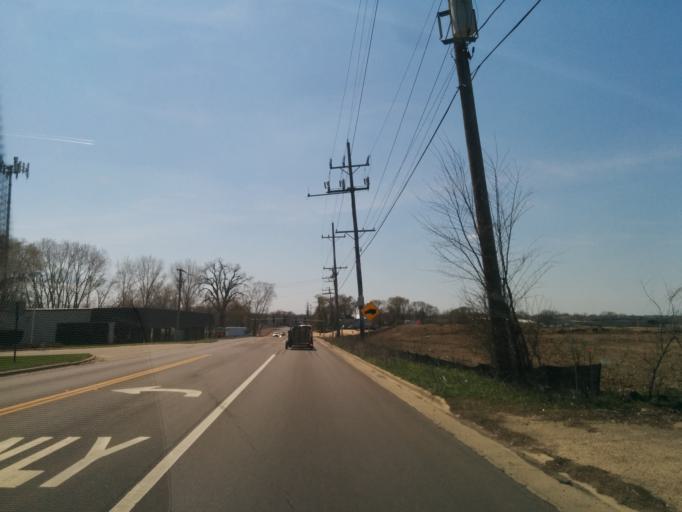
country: US
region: Illinois
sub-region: Kane County
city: South Elgin
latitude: 42.0115
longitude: -88.2884
